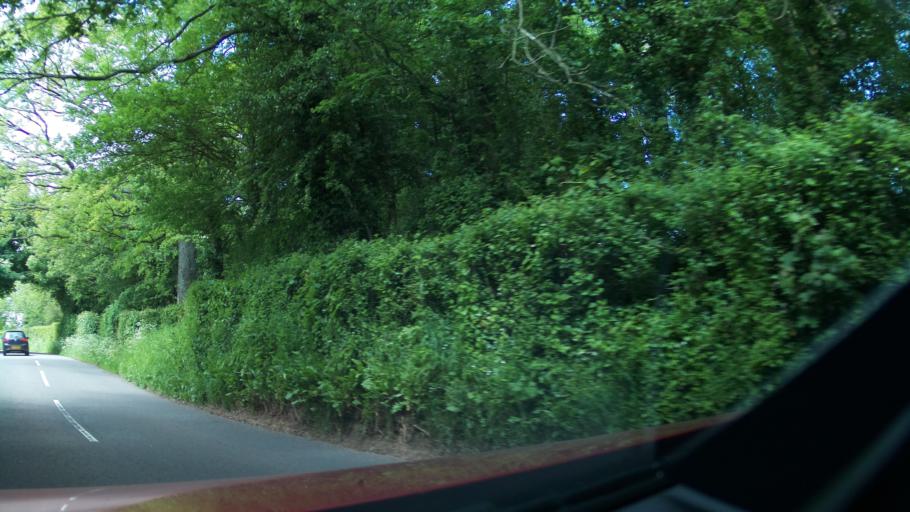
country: GB
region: England
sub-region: Herefordshire
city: Llanrothal
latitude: 51.8616
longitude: -2.8129
